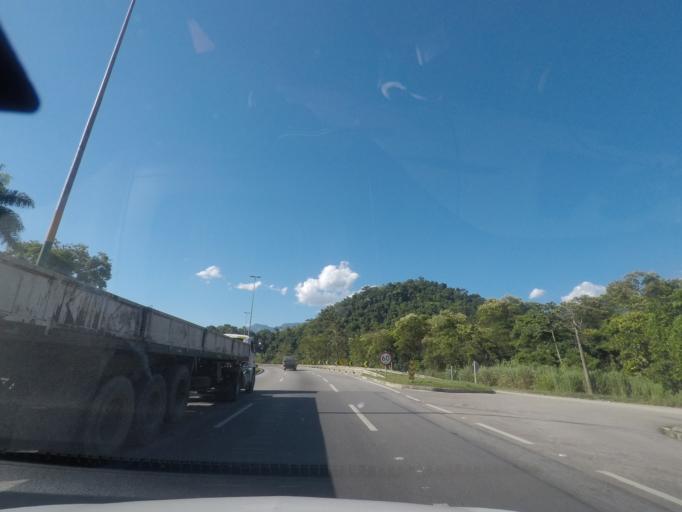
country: BR
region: Rio de Janeiro
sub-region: Petropolis
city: Petropolis
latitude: -22.6602
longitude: -43.1164
